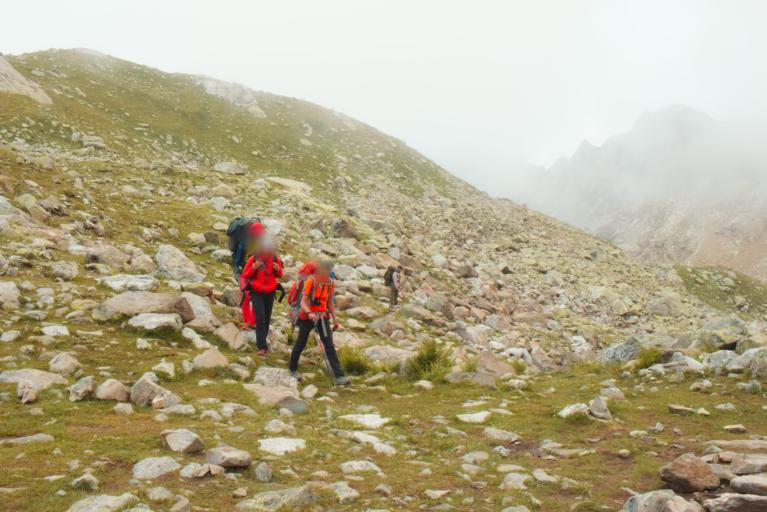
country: RU
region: Karachayevo-Cherkesiya
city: Nizhniy Arkhyz
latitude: 43.4512
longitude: 41.2300
